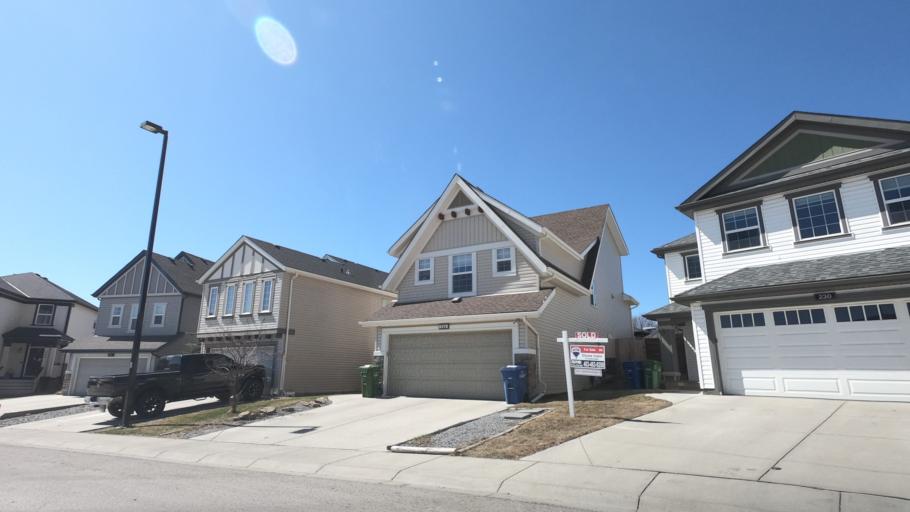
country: CA
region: Alberta
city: Airdrie
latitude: 51.3025
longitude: -114.0478
